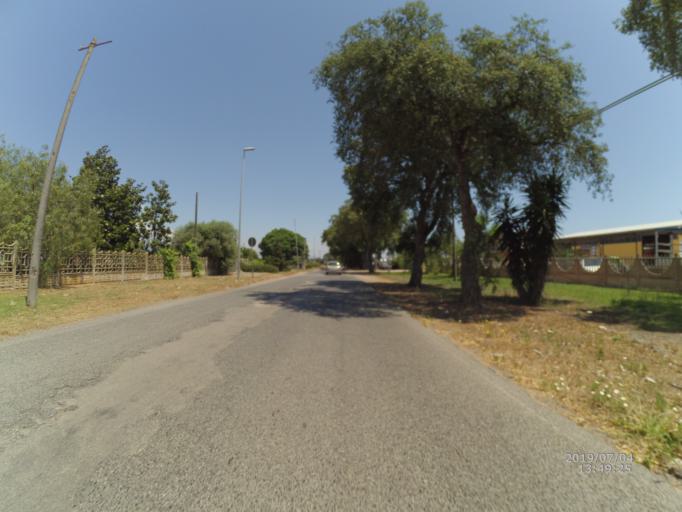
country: IT
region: Latium
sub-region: Provincia di Latina
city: San Felice Circeo
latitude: 41.2853
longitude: 13.1132
